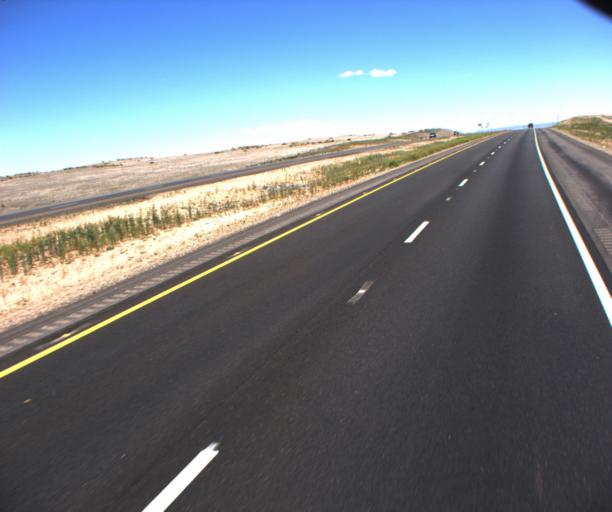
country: US
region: Arizona
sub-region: Yavapai County
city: Chino Valley
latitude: 34.6786
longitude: -112.4425
